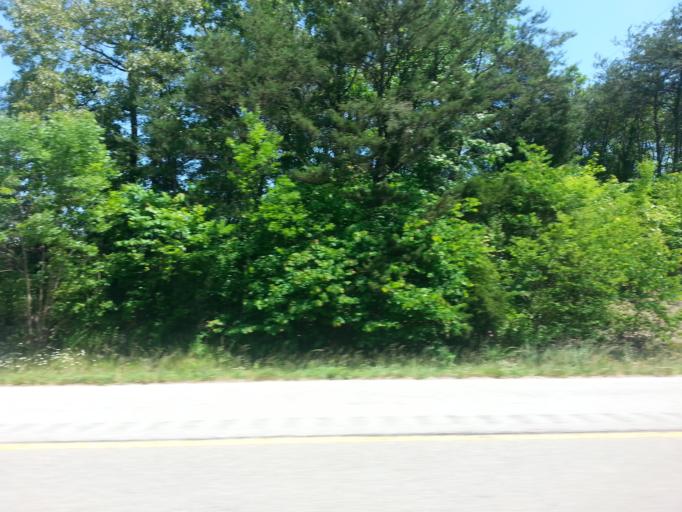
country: US
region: Tennessee
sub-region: Knox County
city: Mascot
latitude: 35.9892
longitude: -83.6606
